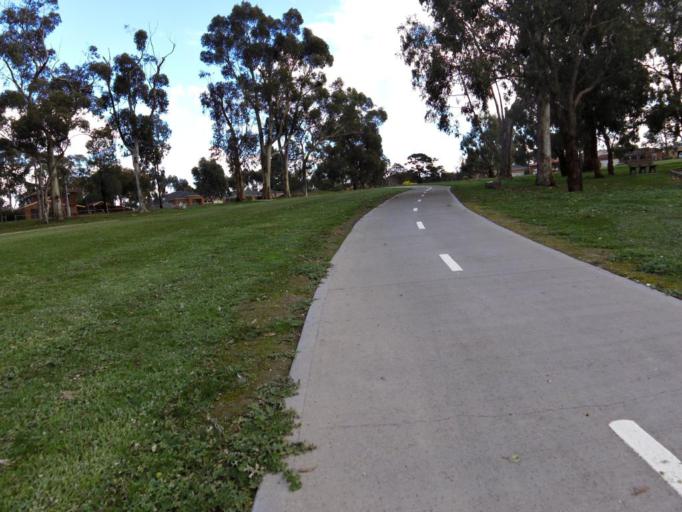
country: AU
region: Victoria
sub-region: Banyule
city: Watsonia North
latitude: -37.6886
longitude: 145.0871
